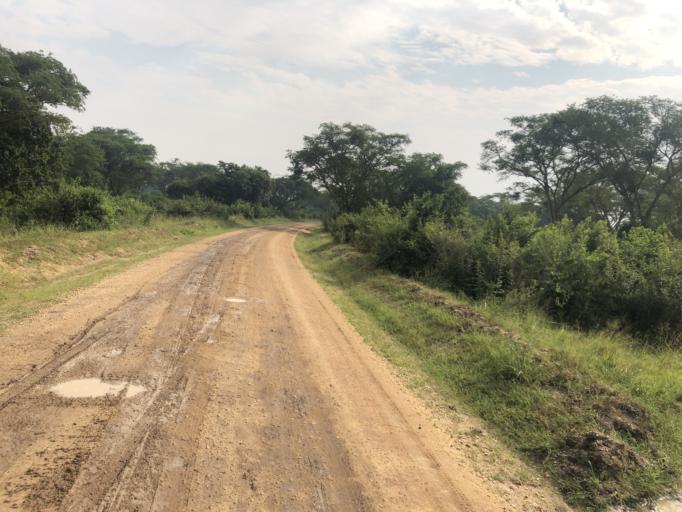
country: UG
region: Western Region
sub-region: Mitoma District
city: Mitoma
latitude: -0.4722
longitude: 29.7962
